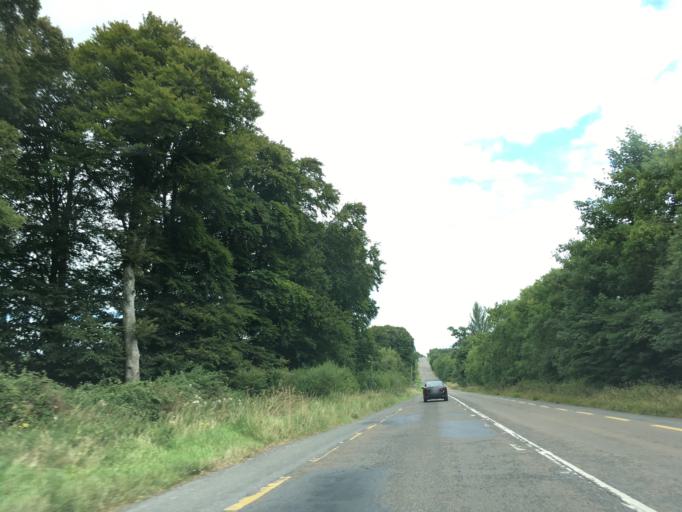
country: IE
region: Munster
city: Cashel
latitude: 52.4819
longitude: -7.8919
